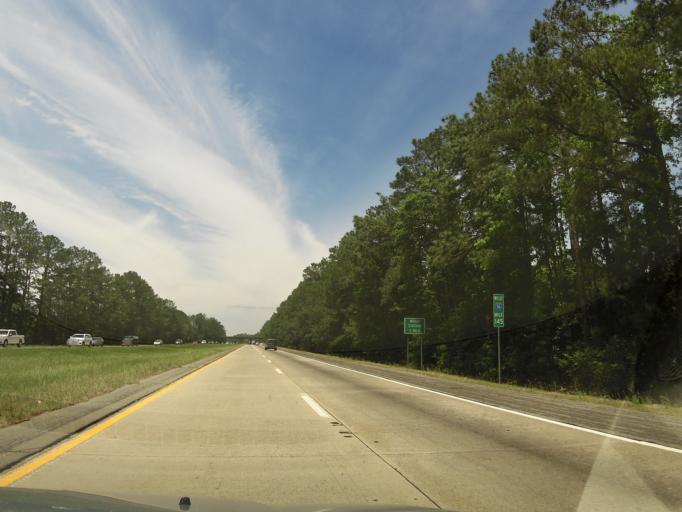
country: US
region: Georgia
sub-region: Chatham County
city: Bloomingdale
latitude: 32.1562
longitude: -81.4294
